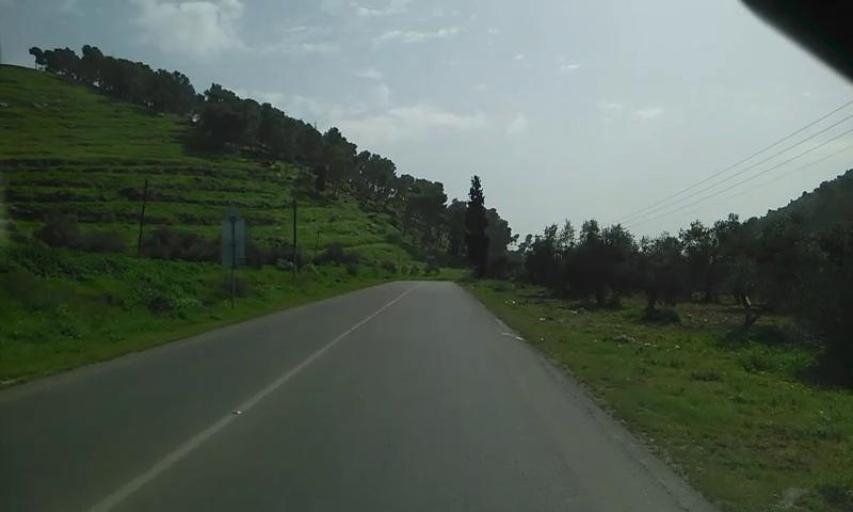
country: PS
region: West Bank
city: Mirkah
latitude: 32.4018
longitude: 35.2252
